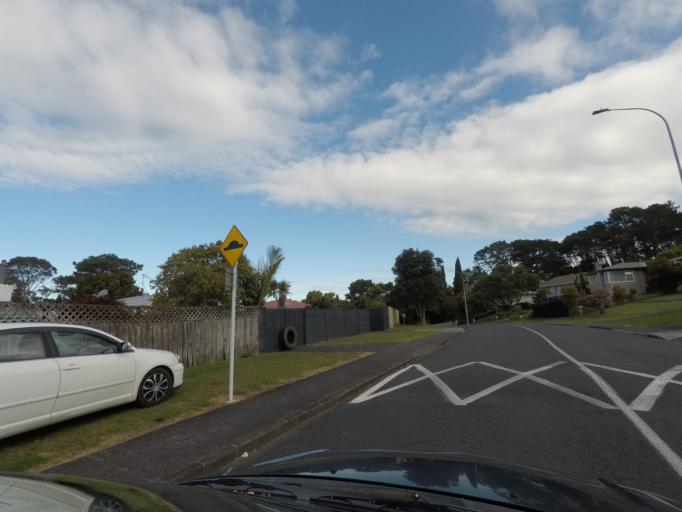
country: NZ
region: Auckland
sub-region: Auckland
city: Rosebank
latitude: -36.8882
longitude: 174.6517
